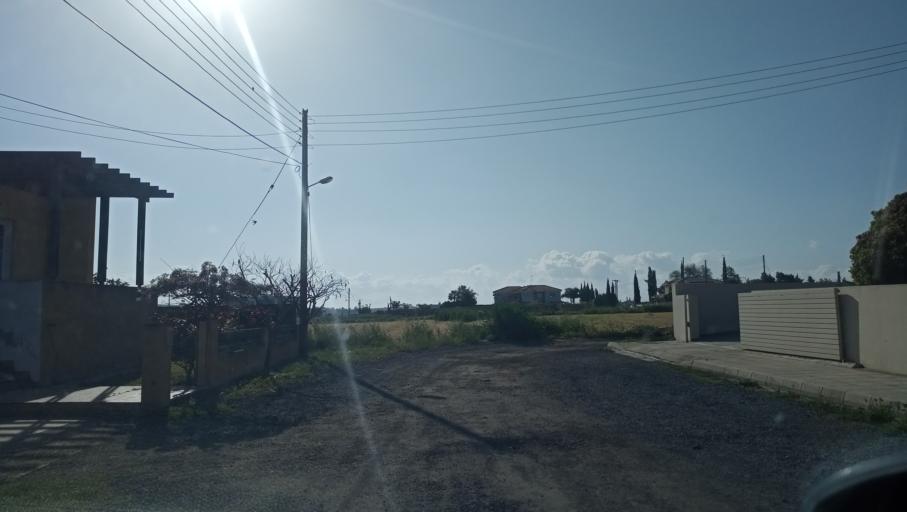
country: CY
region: Lefkosia
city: Tseri
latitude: 35.0792
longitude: 33.3158
